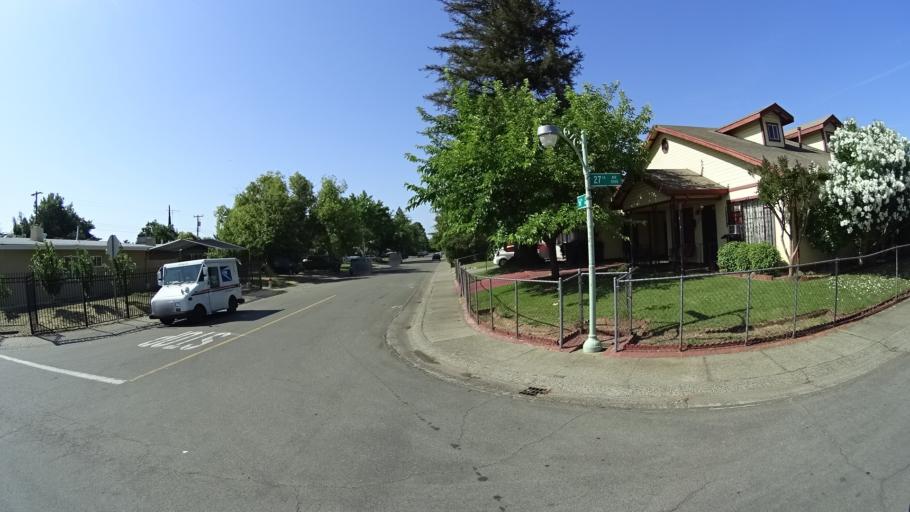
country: US
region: California
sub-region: Sacramento County
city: Parkway
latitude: 38.5272
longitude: -121.4405
